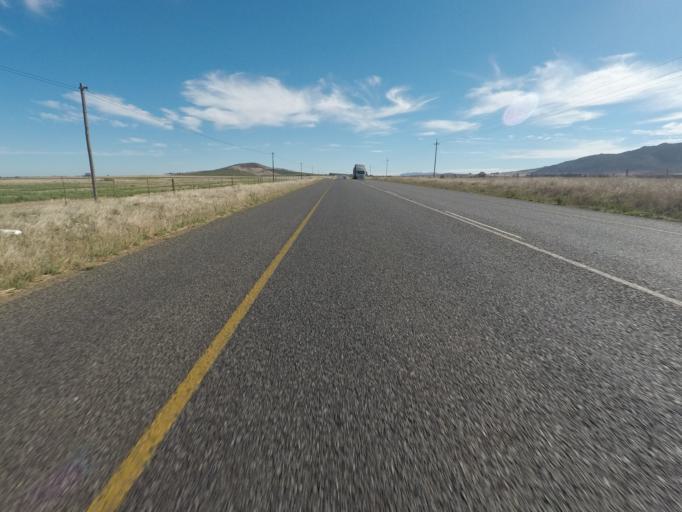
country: ZA
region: Western Cape
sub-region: West Coast District Municipality
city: Malmesbury
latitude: -33.6102
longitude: 18.7278
